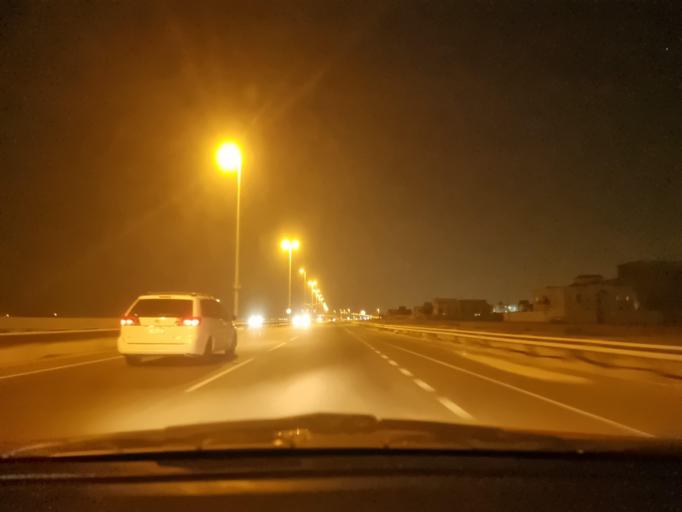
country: AE
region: Abu Dhabi
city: Abu Dhabi
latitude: 24.3674
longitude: 54.6706
